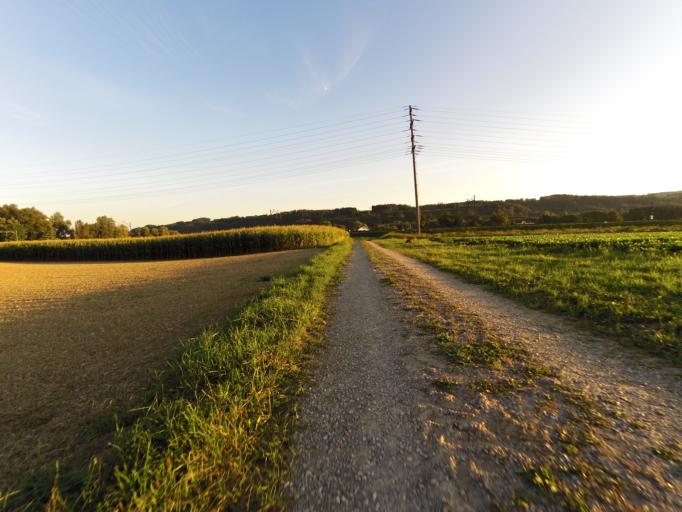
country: CH
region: Thurgau
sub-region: Weinfelden District
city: Wigoltingen
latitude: 47.5881
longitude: 9.0259
